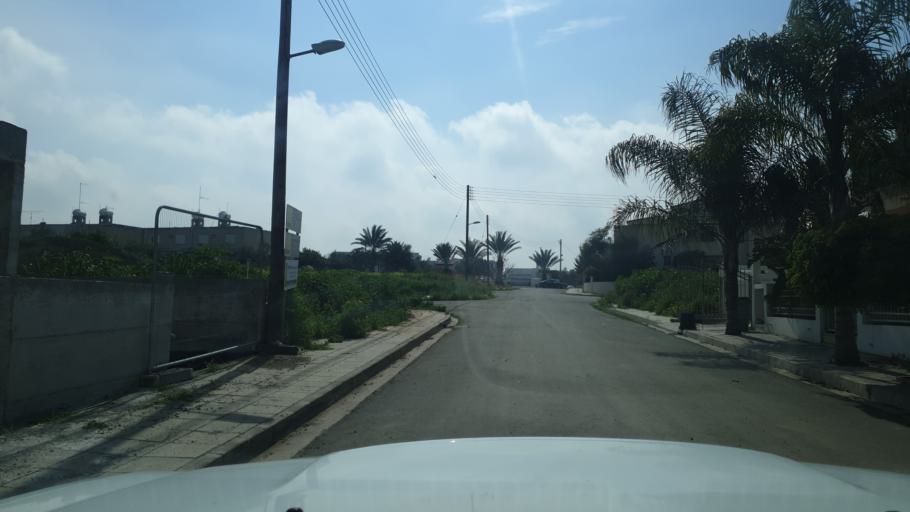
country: CY
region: Lefkosia
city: Kato Deftera
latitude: 35.0881
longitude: 33.2728
